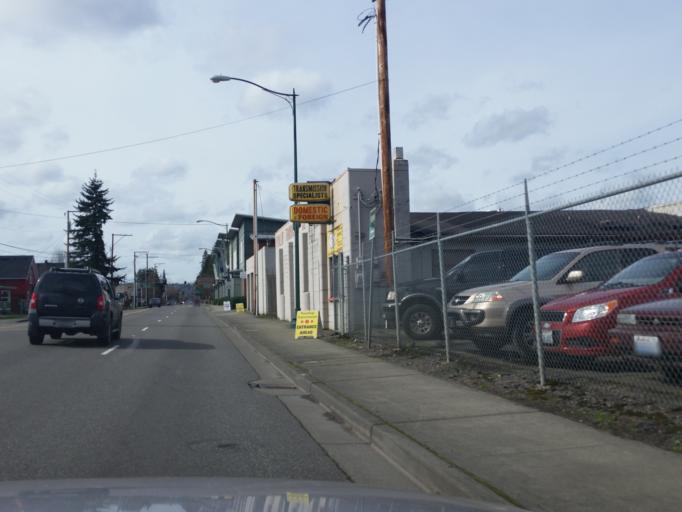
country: US
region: Washington
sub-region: Pierce County
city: Puyallup
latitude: 47.1905
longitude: -122.2855
